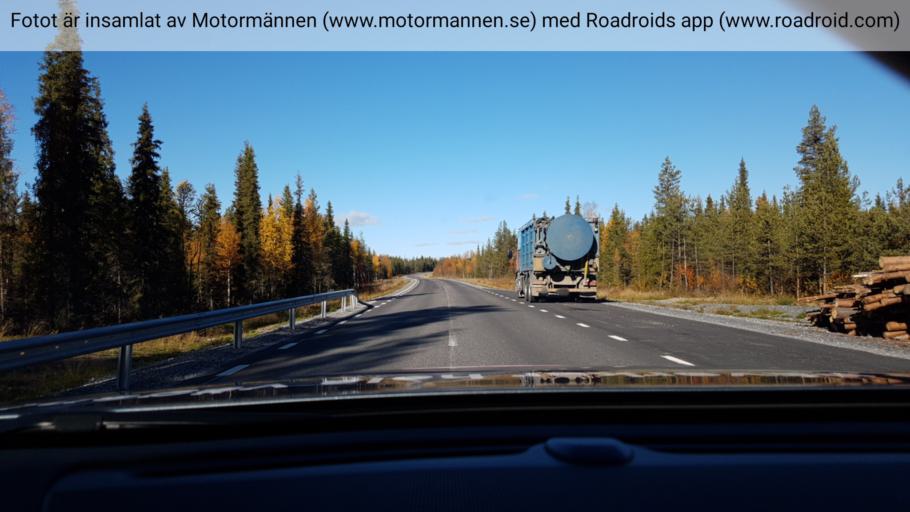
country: SE
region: Norrbotten
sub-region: Gallivare Kommun
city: Gaellivare
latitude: 66.8545
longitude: 20.9994
